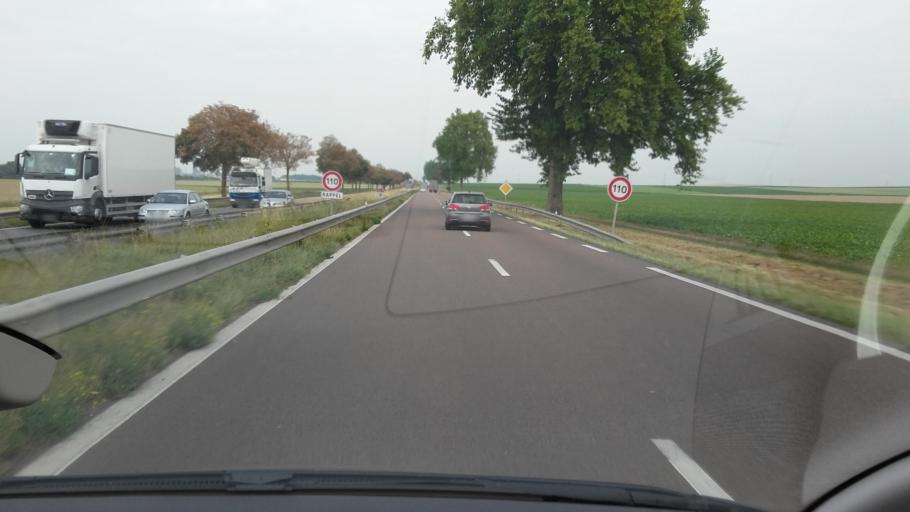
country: FR
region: Champagne-Ardenne
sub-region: Departement de la Marne
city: Witry-les-Reims
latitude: 49.3183
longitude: 4.1550
